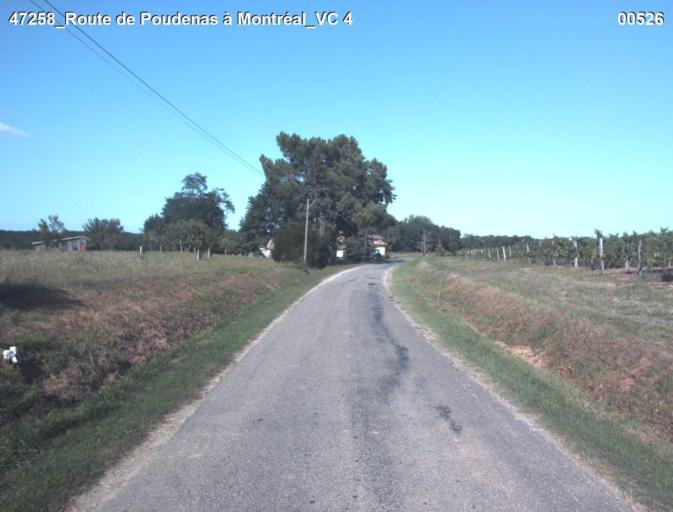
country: FR
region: Midi-Pyrenees
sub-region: Departement du Gers
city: Montreal
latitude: 44.0086
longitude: 0.1838
